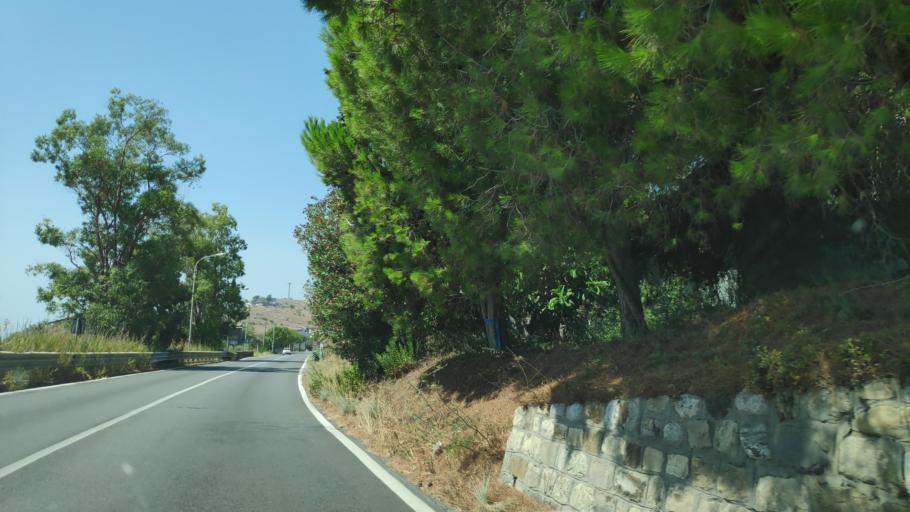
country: IT
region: Calabria
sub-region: Provincia di Reggio Calabria
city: Africo Nuovo
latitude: 38.0226
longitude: 16.1379
